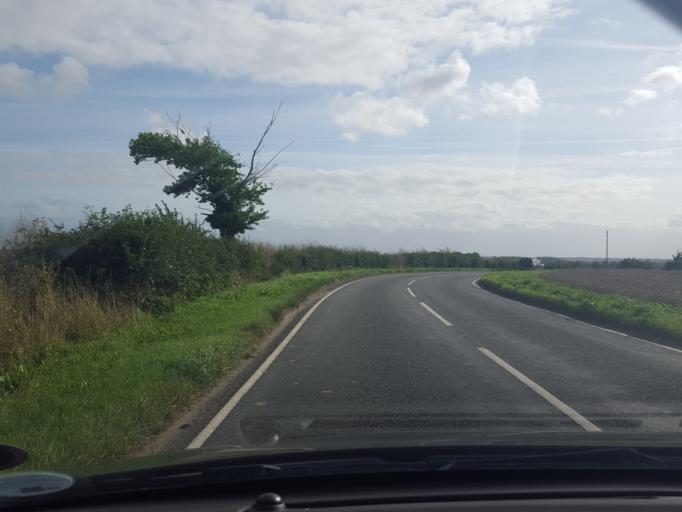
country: GB
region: England
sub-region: Essex
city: Dovercourt
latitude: 51.9118
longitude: 1.2208
